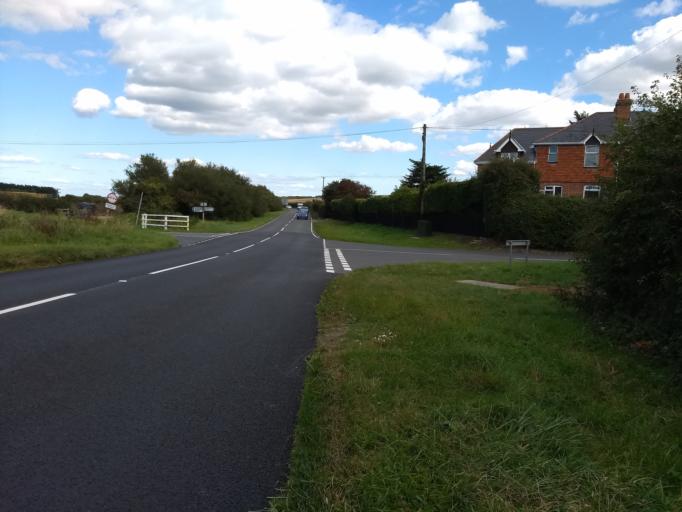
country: GB
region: England
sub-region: Isle of Wight
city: Shalfleet
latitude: 50.6713
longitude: -1.4395
